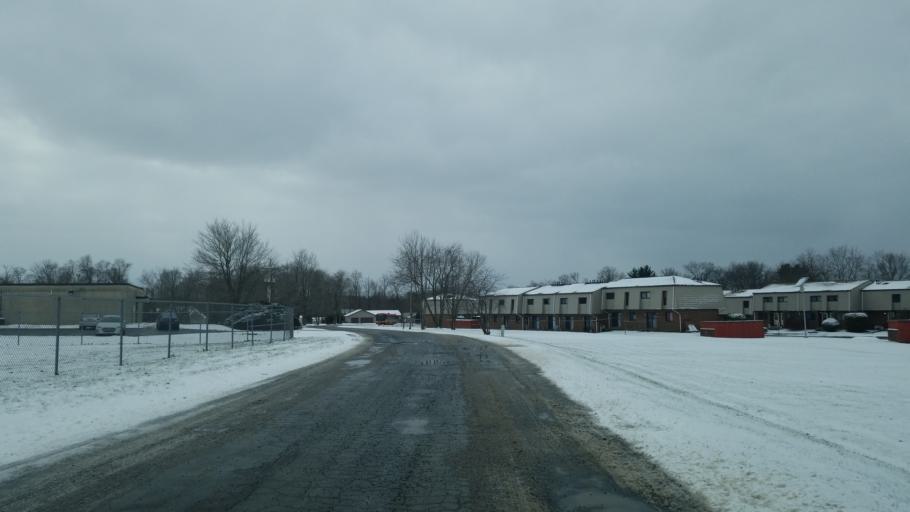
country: US
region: Pennsylvania
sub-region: Clearfield County
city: DuBois
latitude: 41.1103
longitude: -78.7328
